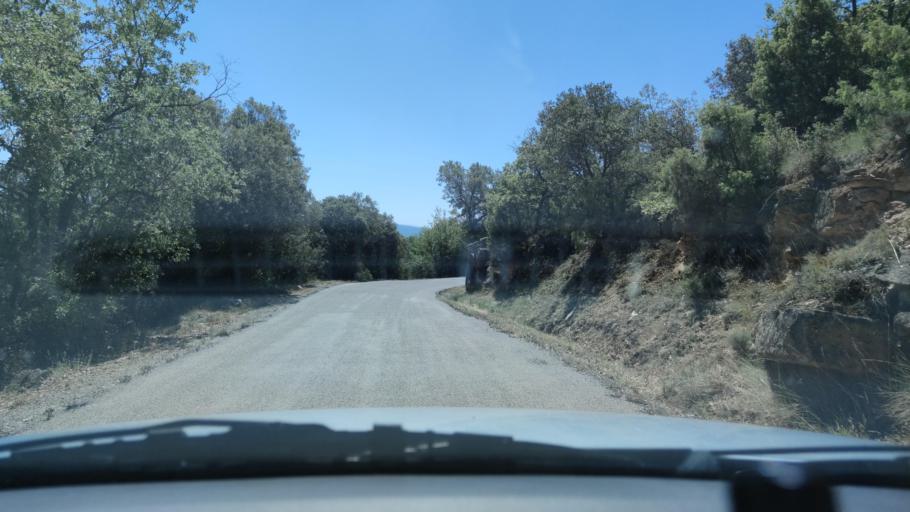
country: ES
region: Catalonia
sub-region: Provincia de Lleida
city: Tora de Riubregos
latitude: 41.8748
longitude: 1.4360
